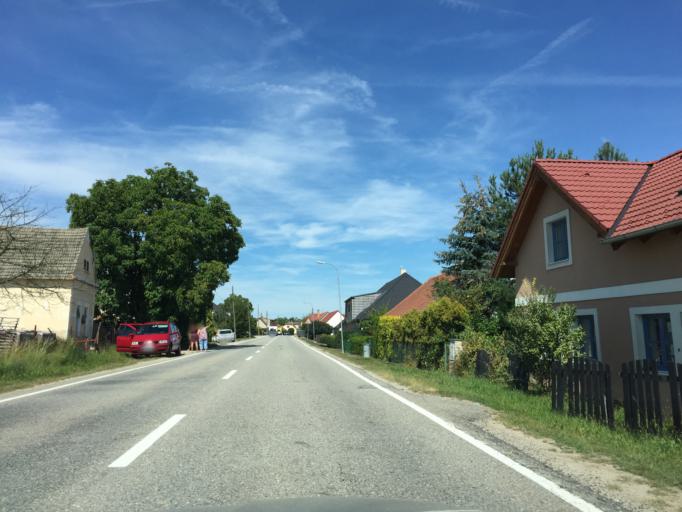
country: CZ
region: Jihocesky
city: Sevetin
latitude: 49.0867
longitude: 14.5430
